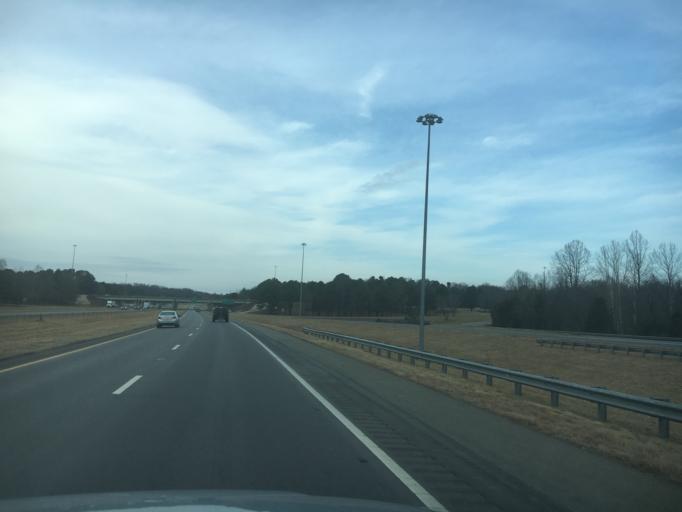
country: US
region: North Carolina
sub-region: Catawba County
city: Mountain View
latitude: 35.7036
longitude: -81.3518
